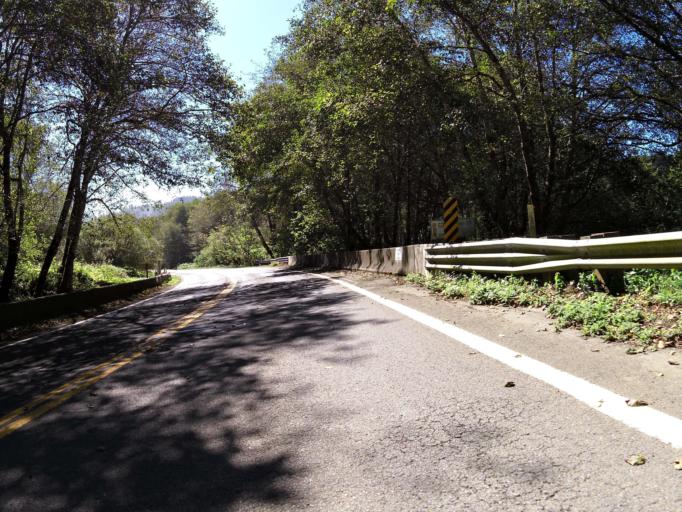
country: US
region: California
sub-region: Mendocino County
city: Fort Bragg
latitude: 39.7771
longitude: -123.8328
